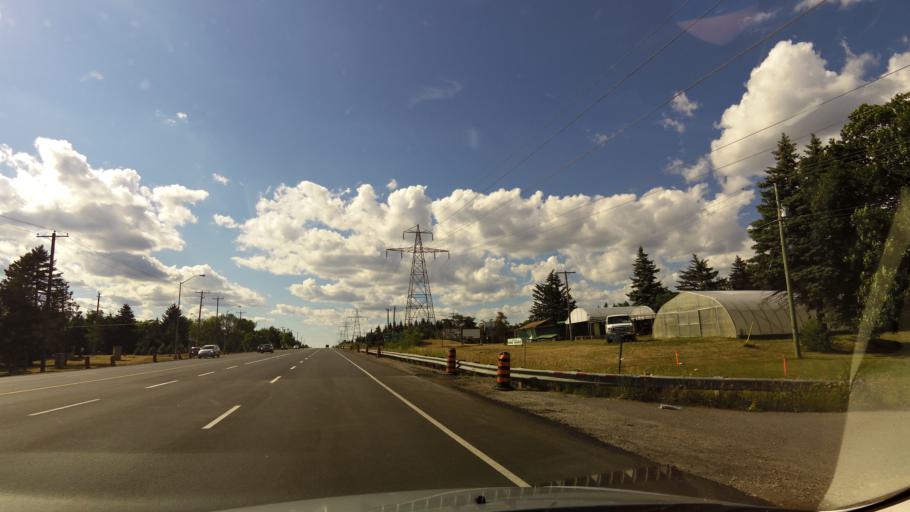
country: CA
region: Ontario
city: Ancaster
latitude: 43.3809
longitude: -80.0112
